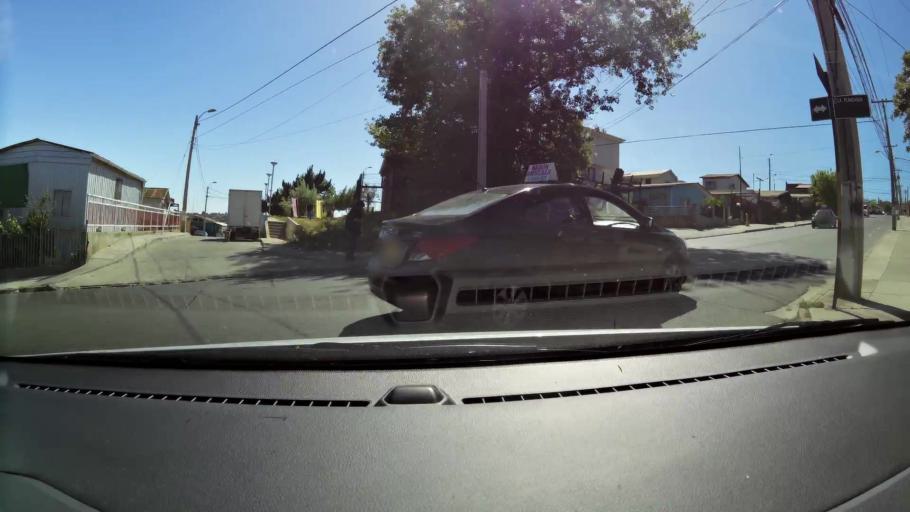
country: CL
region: Valparaiso
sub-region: Provincia de Valparaiso
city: Vina del Mar
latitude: -33.0596
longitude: -71.5757
